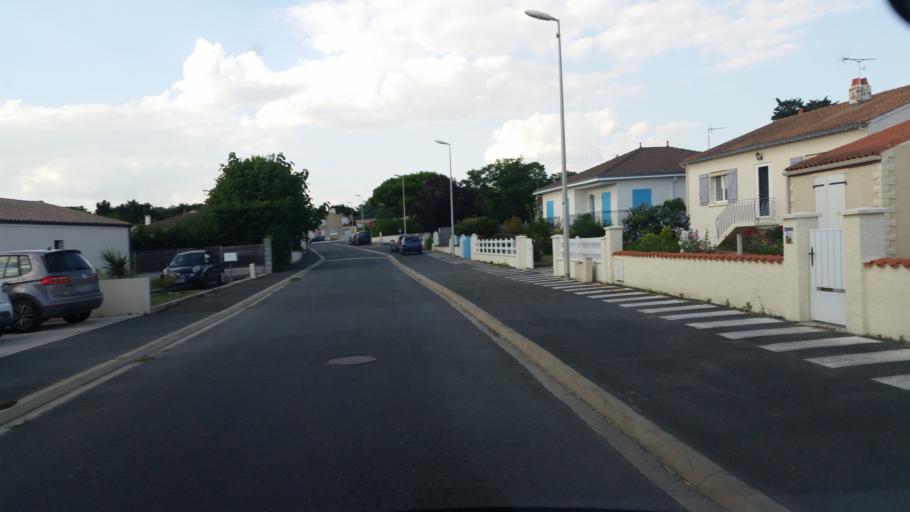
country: FR
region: Poitou-Charentes
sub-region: Departement de la Charente-Maritime
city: Andilly
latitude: 46.2522
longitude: -1.0247
